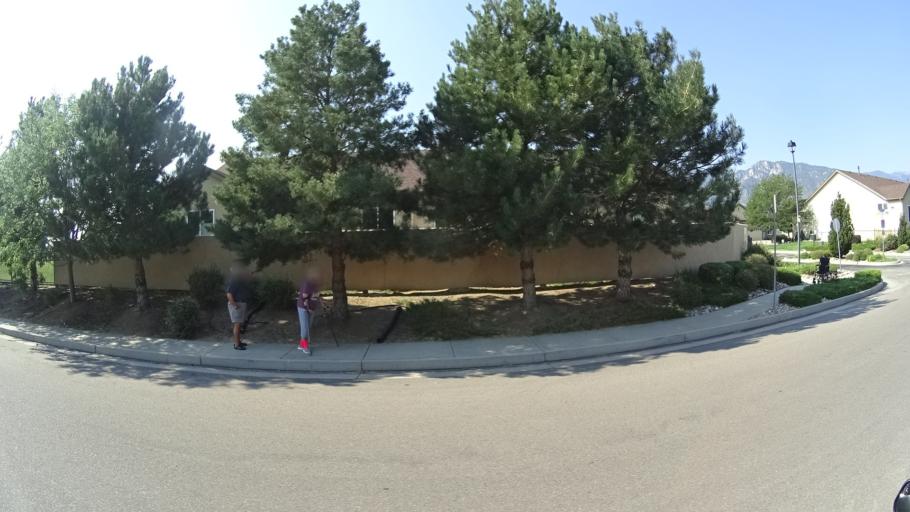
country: US
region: Colorado
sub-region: El Paso County
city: Stratmoor
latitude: 38.7811
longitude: -104.8042
